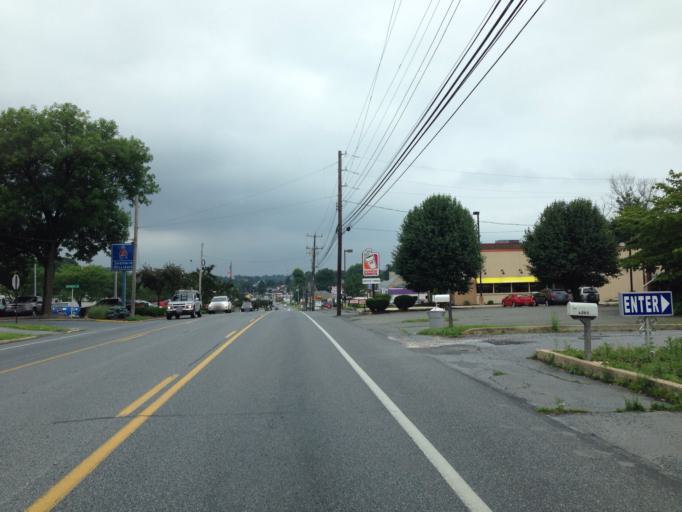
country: US
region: Pennsylvania
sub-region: Lancaster County
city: Millersville
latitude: 40.0386
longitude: -76.3573
